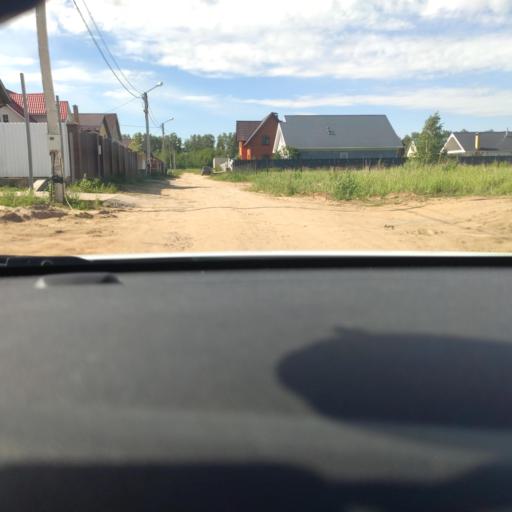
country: RU
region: Tatarstan
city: Vysokaya Gora
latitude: 55.8204
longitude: 49.3088
